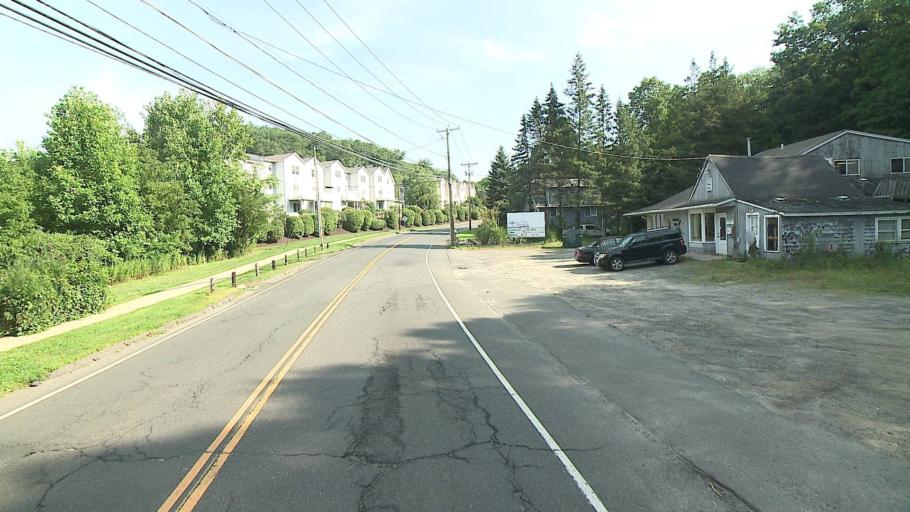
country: US
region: Connecticut
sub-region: Fairfield County
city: Danbury
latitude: 41.4256
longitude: -73.4730
